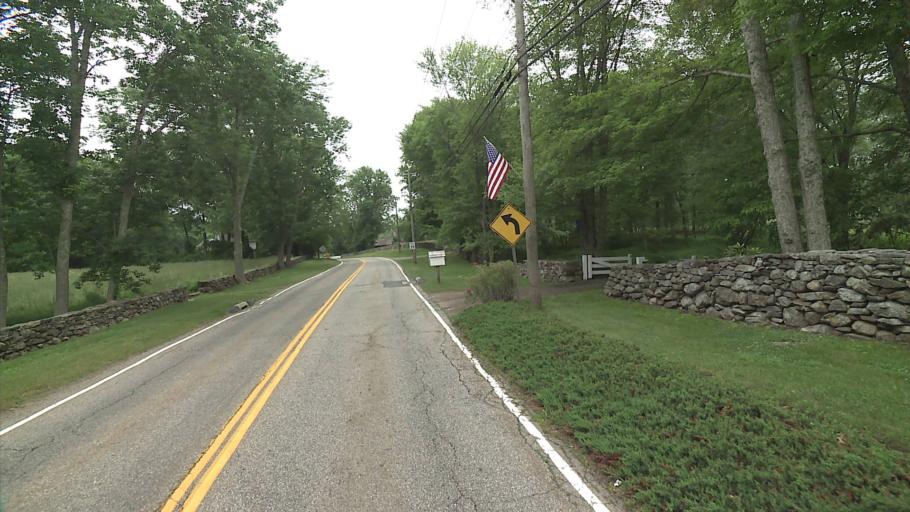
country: US
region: Connecticut
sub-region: Tolland County
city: Coventry Lake
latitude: 41.7357
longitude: -72.3721
